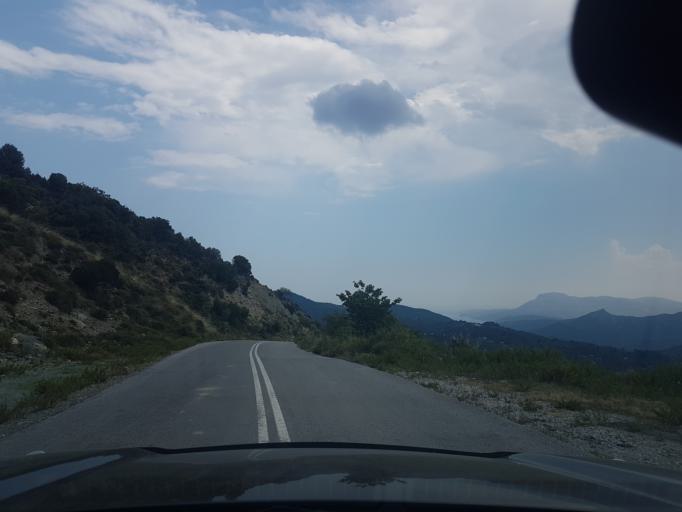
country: GR
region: Central Greece
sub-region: Nomos Evvoias
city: Kymi
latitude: 38.6461
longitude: 24.0554
